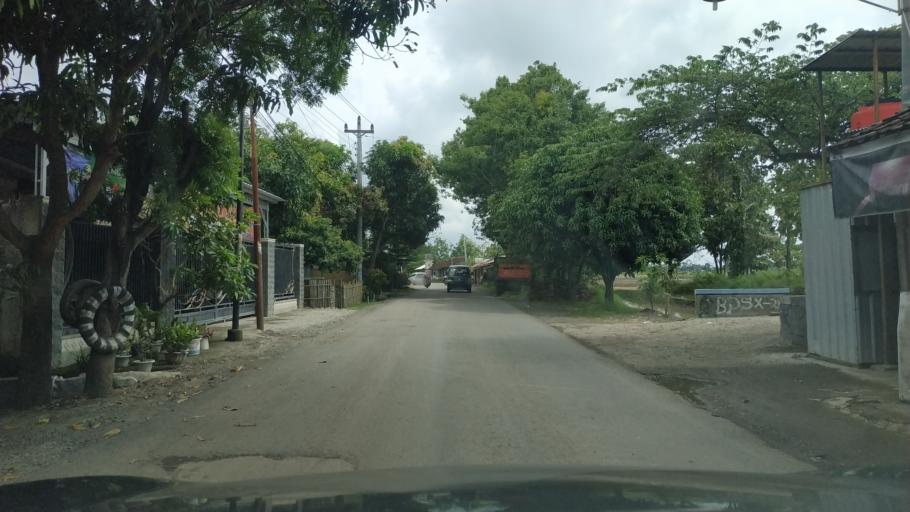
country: ID
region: Central Java
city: Pemalang
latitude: -6.9165
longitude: 109.3277
